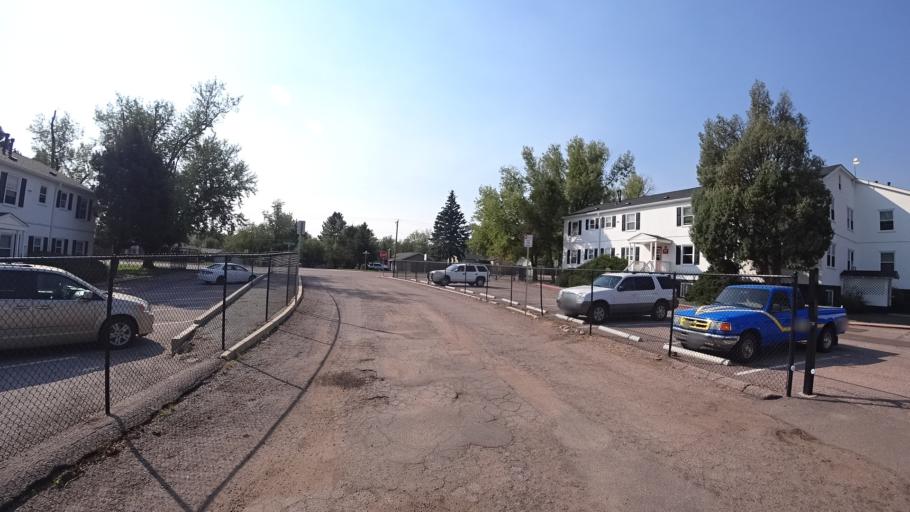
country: US
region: Colorado
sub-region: El Paso County
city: Colorado Springs
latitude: 38.8053
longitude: -104.8372
